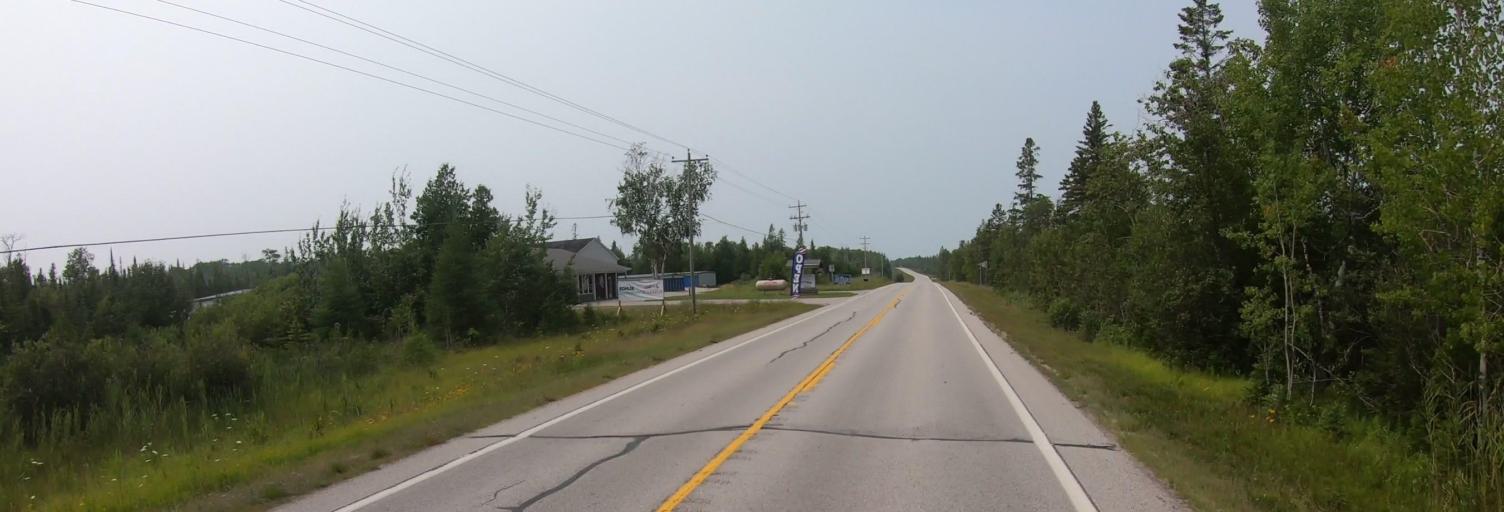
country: CA
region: Ontario
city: Thessalon
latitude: 45.9855
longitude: -83.8125
